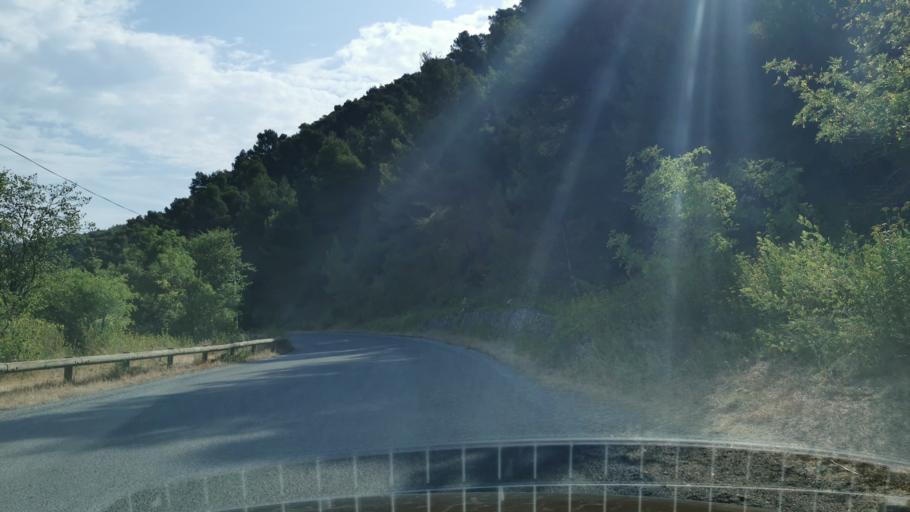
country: FR
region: Languedoc-Roussillon
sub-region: Departement de l'Aude
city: Bize-Minervois
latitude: 43.3179
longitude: 2.8779
